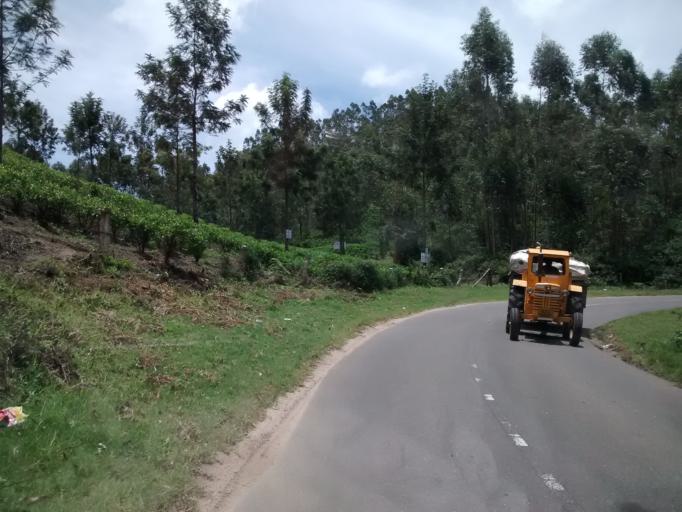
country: IN
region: Kerala
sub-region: Idukki
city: Munnar
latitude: 10.1380
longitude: 77.2043
